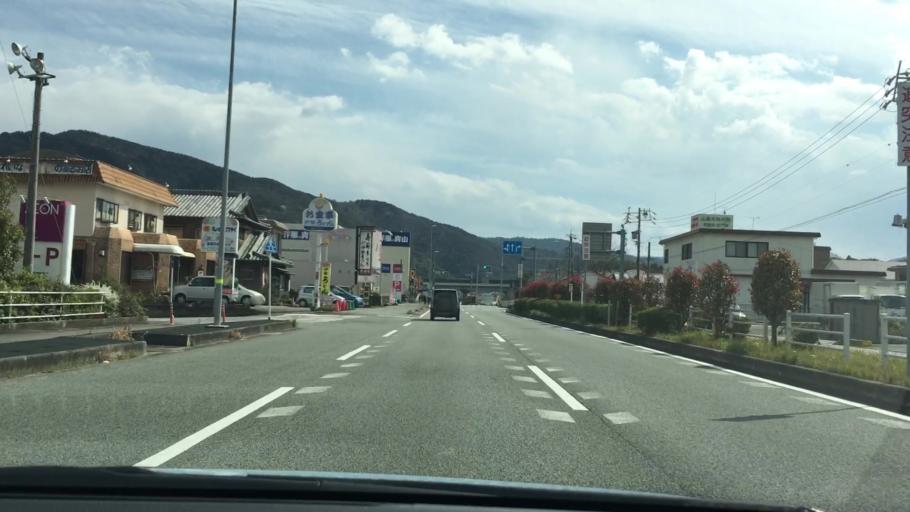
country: JP
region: Mie
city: Ise
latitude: 34.4779
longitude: 136.7298
